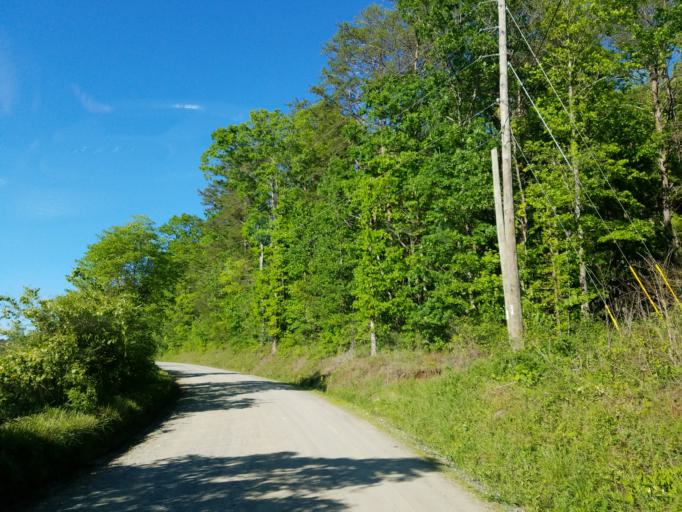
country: US
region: Georgia
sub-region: Gilmer County
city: Ellijay
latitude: 34.6054
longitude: -84.5062
